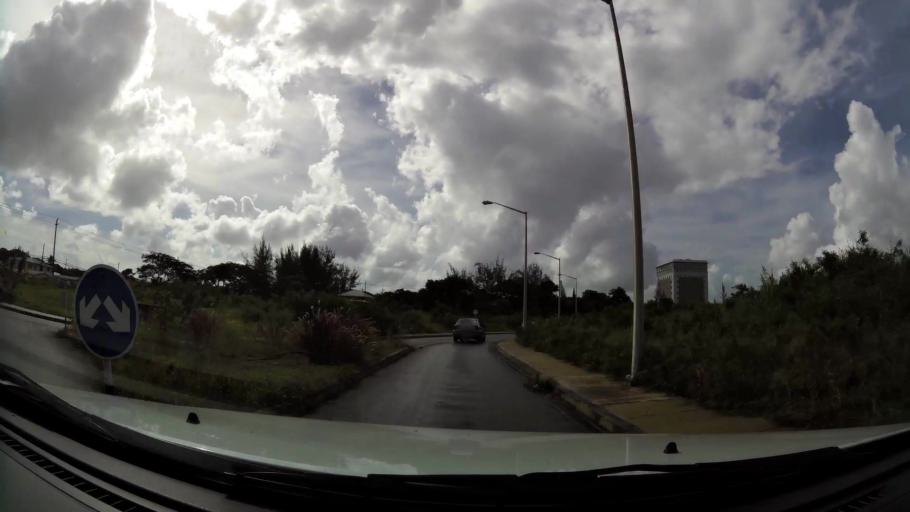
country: BB
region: Saint Michael
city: Bridgetown
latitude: 13.1395
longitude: -59.6094
